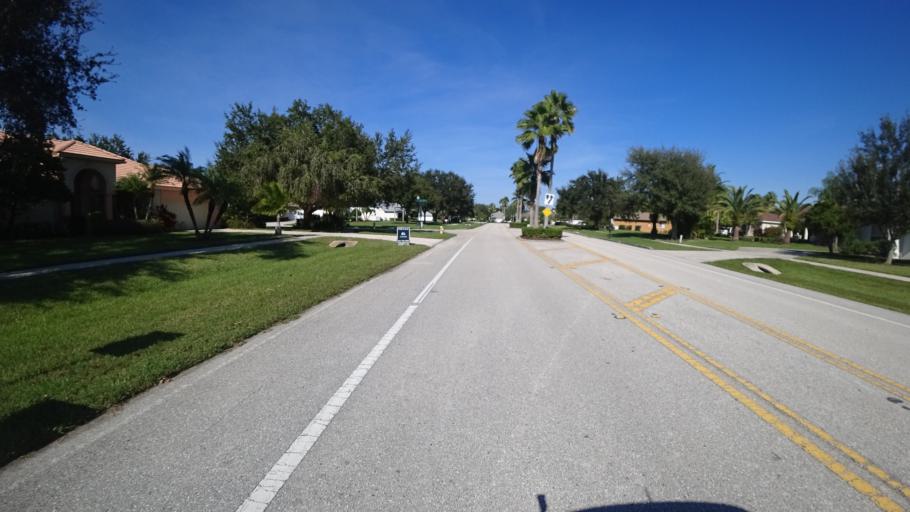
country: US
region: Florida
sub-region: Sarasota County
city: The Meadows
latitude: 27.4133
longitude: -82.4378
